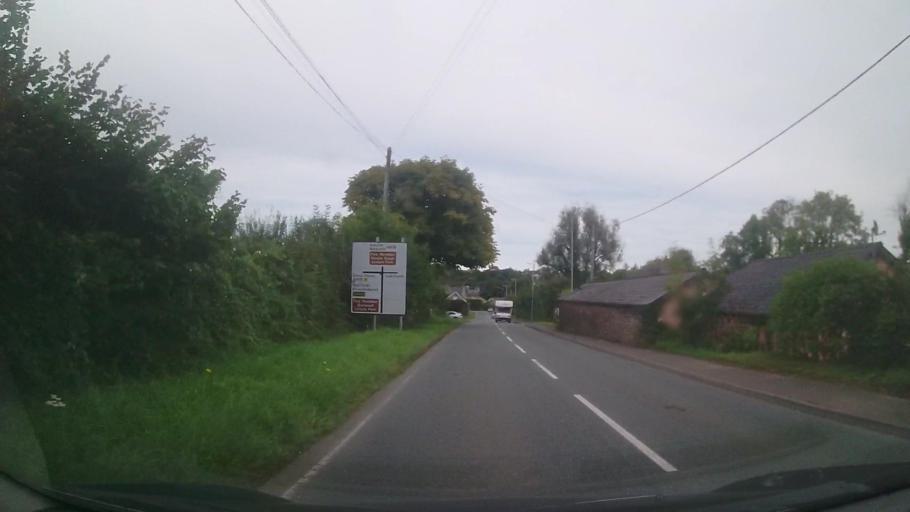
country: GB
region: Wales
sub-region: Pembrokeshire
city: Templeton
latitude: 51.7668
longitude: -4.7370
